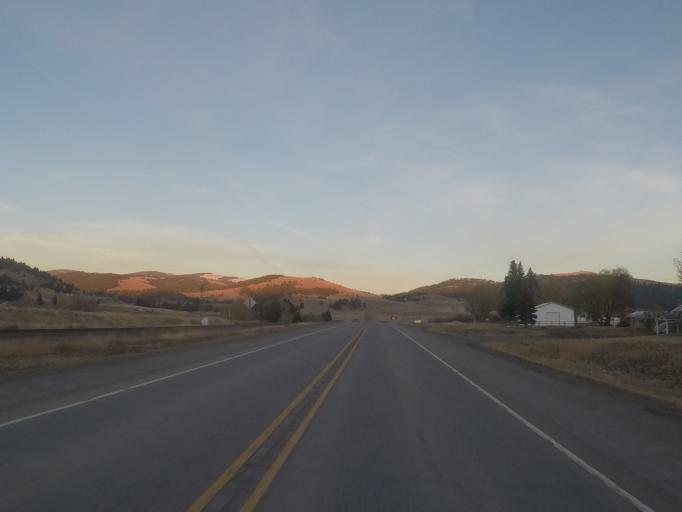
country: US
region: Montana
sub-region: Lewis and Clark County
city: Helena West Side
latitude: 46.5567
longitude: -112.4047
